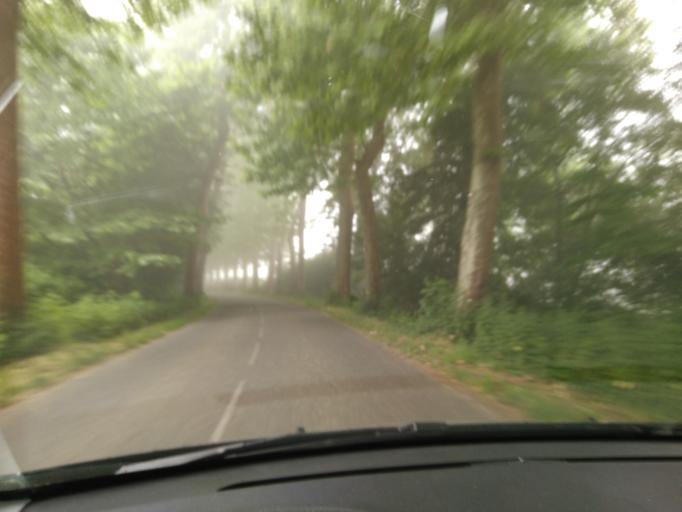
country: FR
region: Midi-Pyrenees
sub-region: Departement du Gers
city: Le Houga
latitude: 43.8606
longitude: -0.1688
